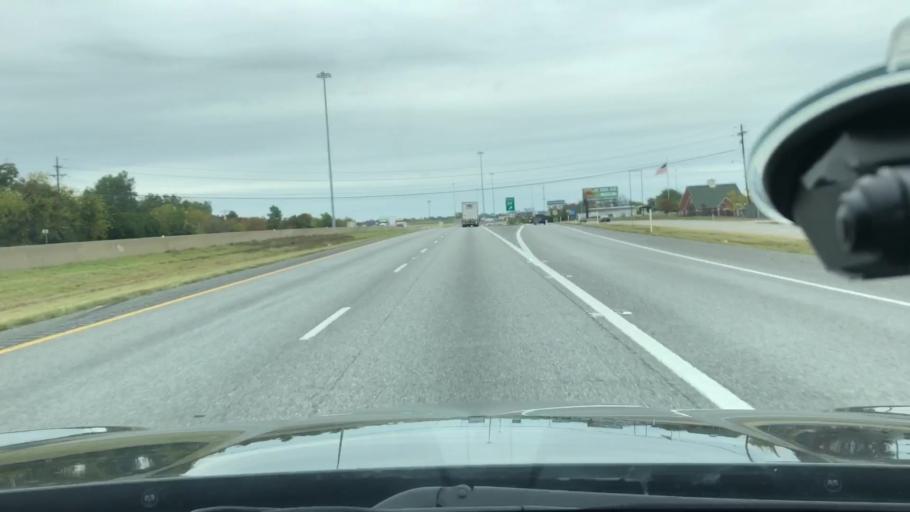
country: US
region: Texas
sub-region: Hunt County
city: Greenville
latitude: 33.1070
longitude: -96.1028
